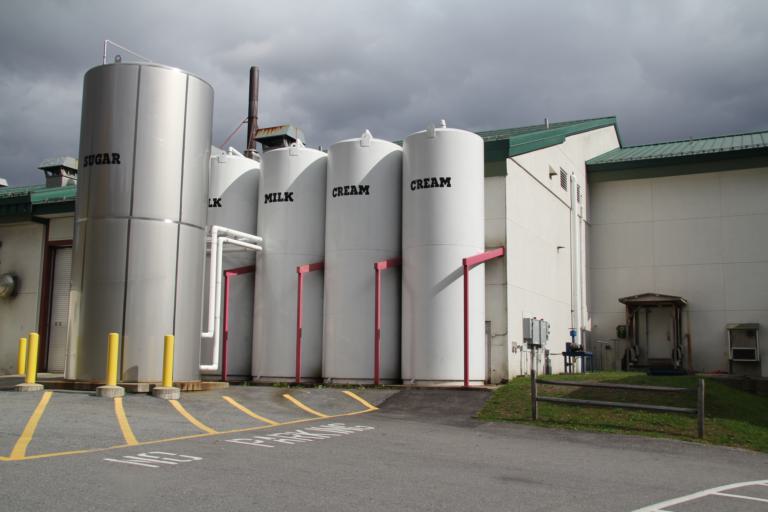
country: US
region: Vermont
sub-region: Washington County
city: Waterbury
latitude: 44.3529
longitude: -72.7402
